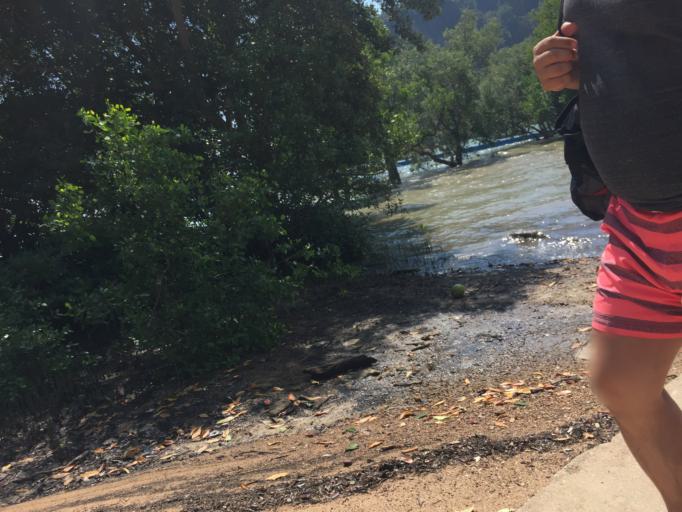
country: TH
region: Phangnga
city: Ban Ao Nang
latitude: 8.0109
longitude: 98.8416
